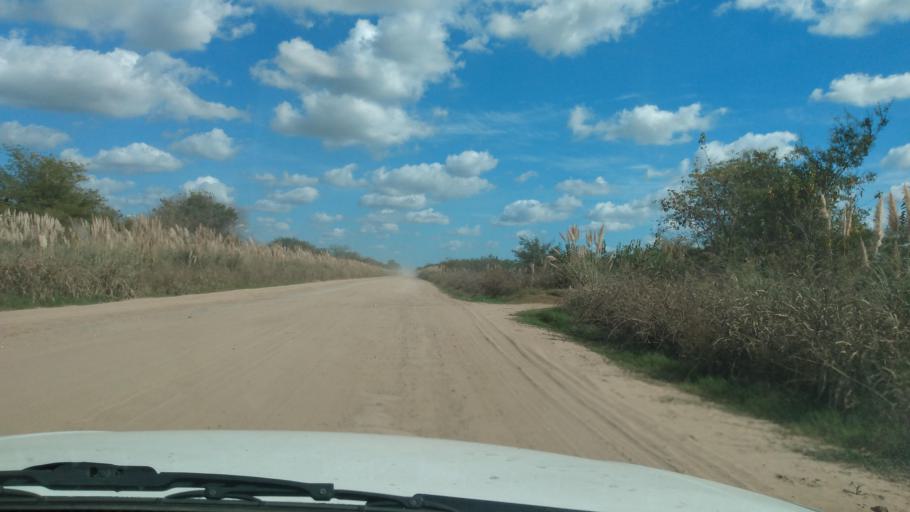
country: AR
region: Buenos Aires
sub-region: Partido de Navarro
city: Navarro
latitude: -34.9985
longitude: -59.3255
